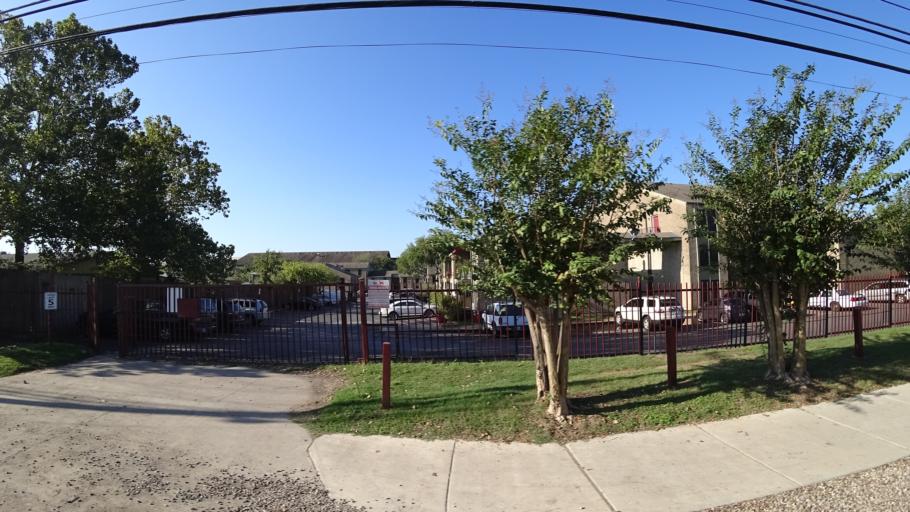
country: US
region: Texas
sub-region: Travis County
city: Austin
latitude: 30.3455
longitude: -97.7029
